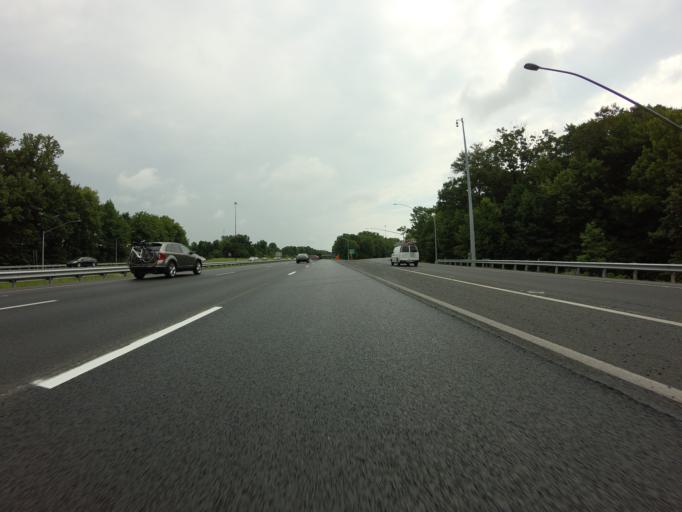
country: US
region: Maryland
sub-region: Harford County
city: Havre de Grace
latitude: 39.5677
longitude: -76.1406
